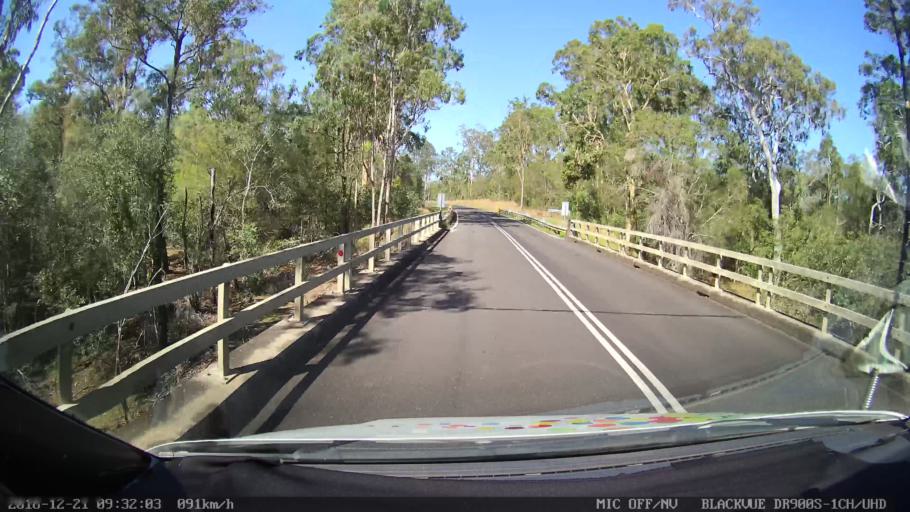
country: AU
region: New South Wales
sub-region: Clarence Valley
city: Maclean
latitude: -29.4660
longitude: 152.9816
